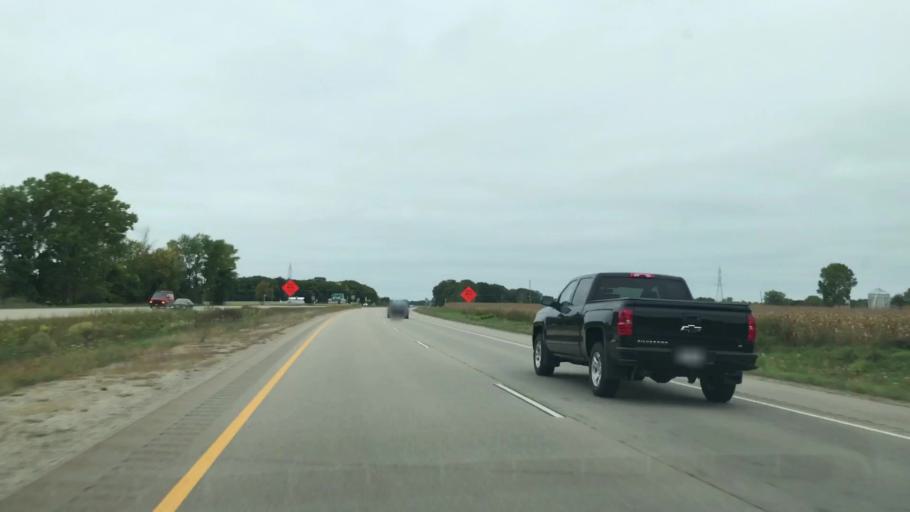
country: US
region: Wisconsin
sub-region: Oconto County
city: Oconto
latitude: 44.8011
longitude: -87.9902
